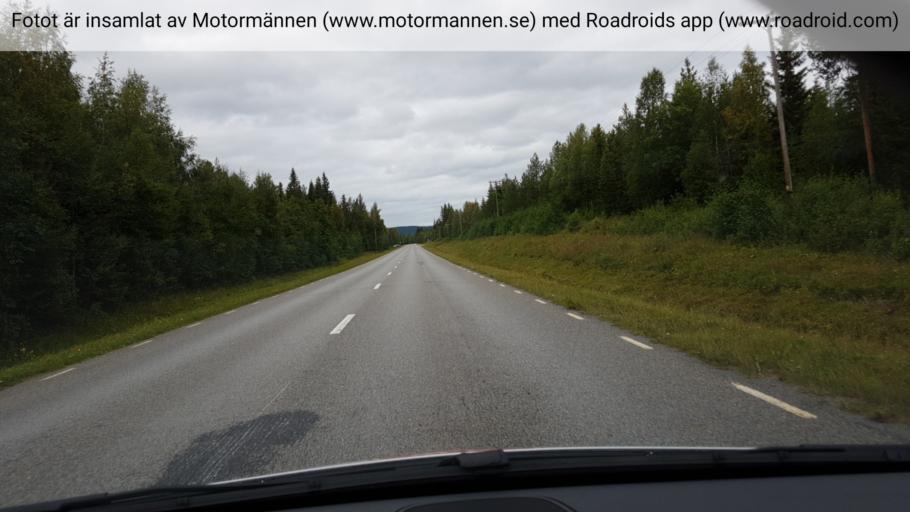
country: SE
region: Jaemtland
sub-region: Stroemsunds Kommun
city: Stroemsund
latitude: 64.2966
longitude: 15.3287
